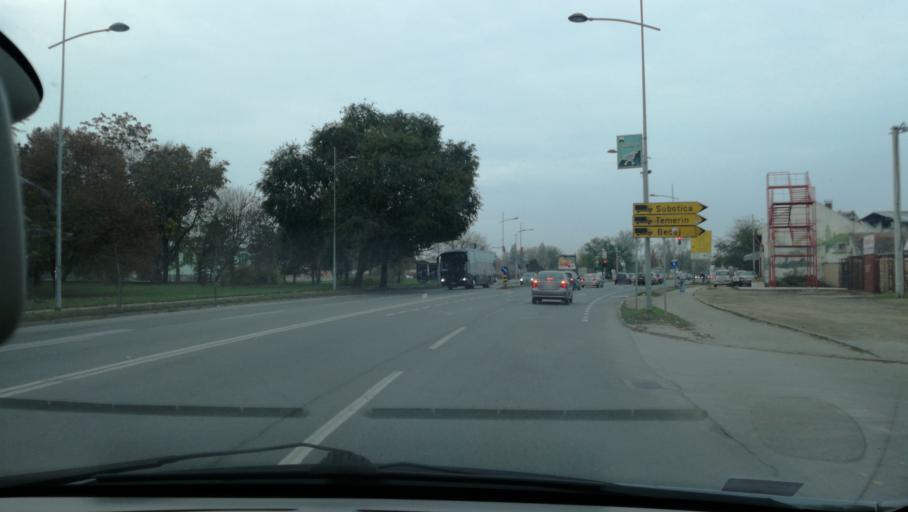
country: RS
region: Autonomna Pokrajina Vojvodina
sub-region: Juznobacki Okrug
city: Novi Sad
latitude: 45.2680
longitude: 19.8324
